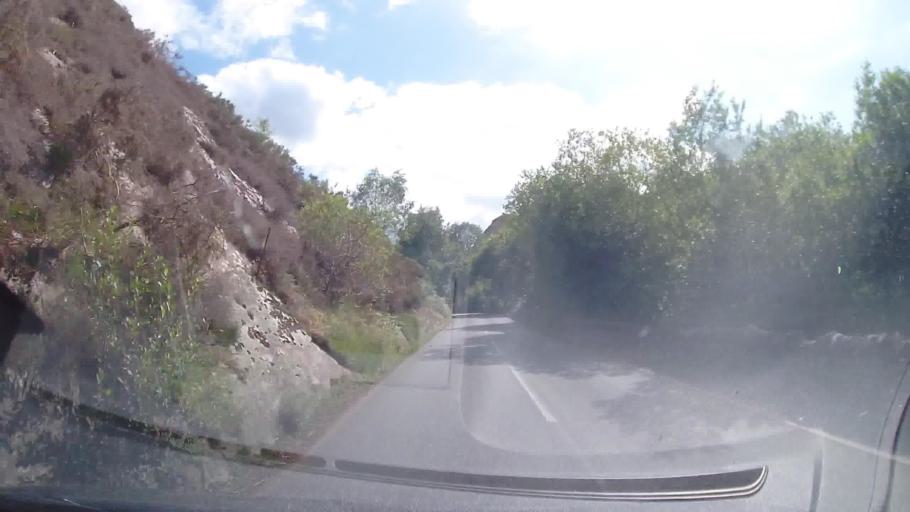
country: GB
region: Wales
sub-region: Gwynedd
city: Penrhyndeudraeth
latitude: 52.9247
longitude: -4.0452
